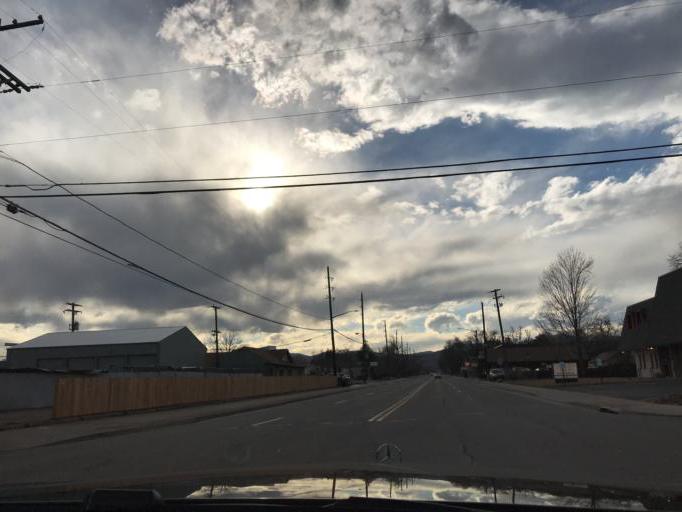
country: US
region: Colorado
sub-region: Jefferson County
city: Arvada
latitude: 39.7782
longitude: -105.1208
